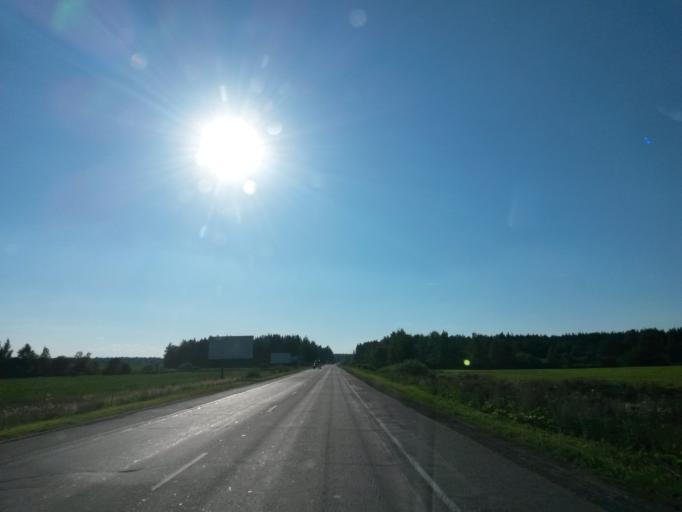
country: RU
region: Ivanovo
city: Novo-Talitsy
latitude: 57.0135
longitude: 40.8148
